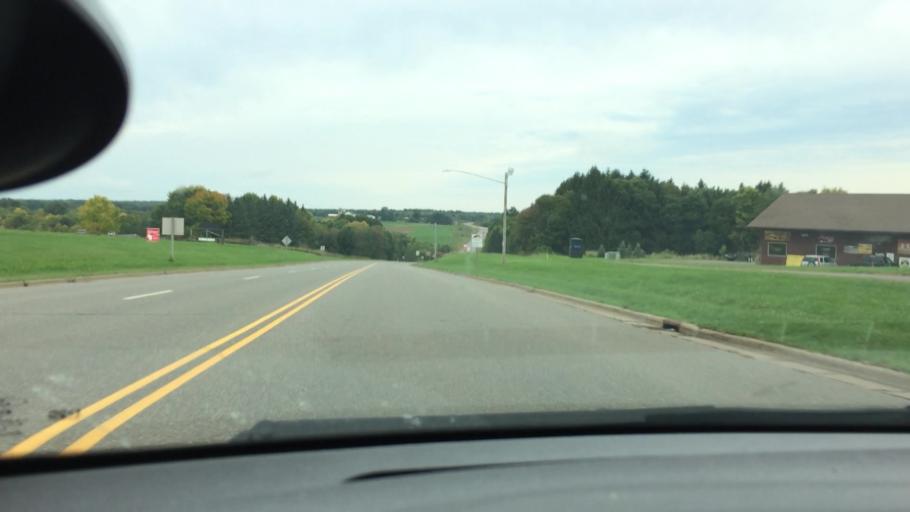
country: US
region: Wisconsin
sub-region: Clark County
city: Neillsville
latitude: 44.5526
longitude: -90.6015
